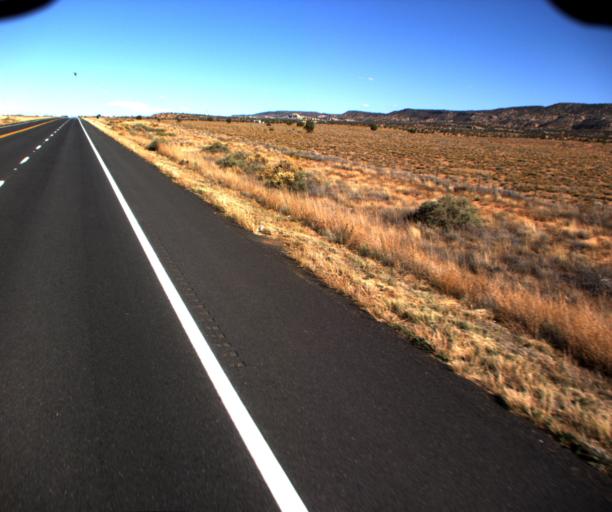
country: US
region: Arizona
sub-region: Coconino County
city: Kaibito
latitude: 36.3986
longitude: -110.8604
